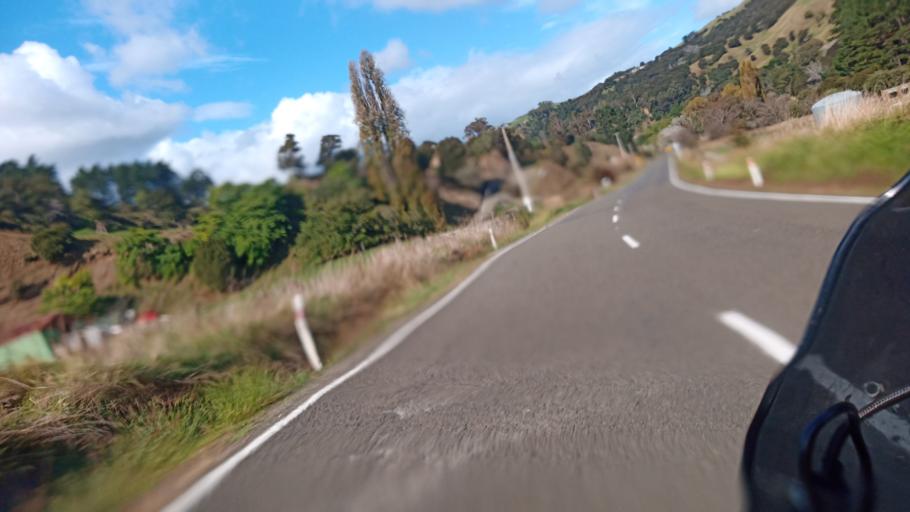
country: NZ
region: Gisborne
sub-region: Gisborne District
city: Gisborne
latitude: -38.4664
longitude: 177.6625
